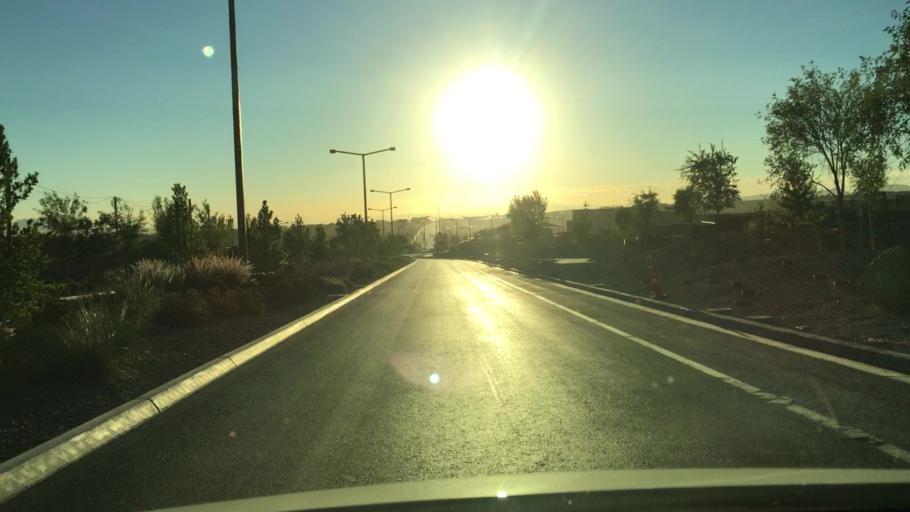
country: US
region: Nevada
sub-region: Clark County
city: Summerlin South
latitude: 36.0626
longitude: -115.3125
